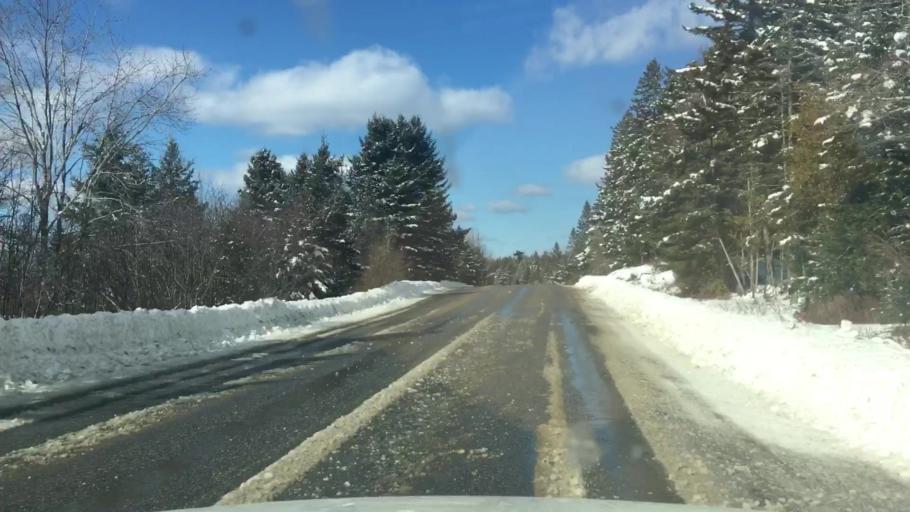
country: US
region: Maine
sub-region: Washington County
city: Machias
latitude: 44.6816
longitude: -67.4560
